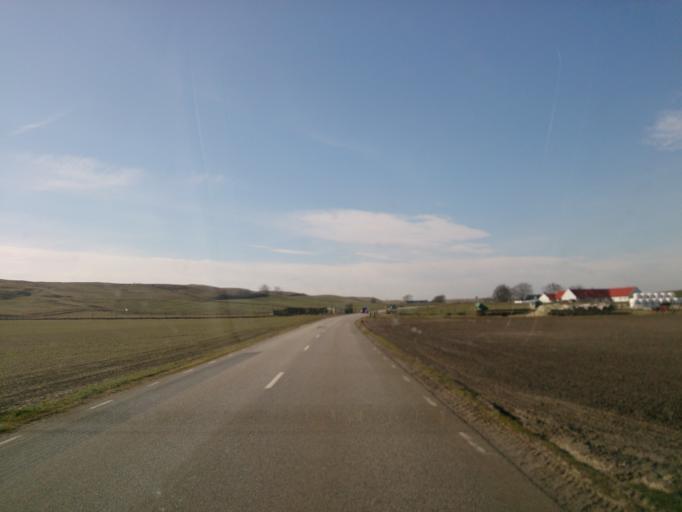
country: SE
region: Skane
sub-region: Ystads Kommun
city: Kopingebro
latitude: 55.3973
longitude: 14.0323
